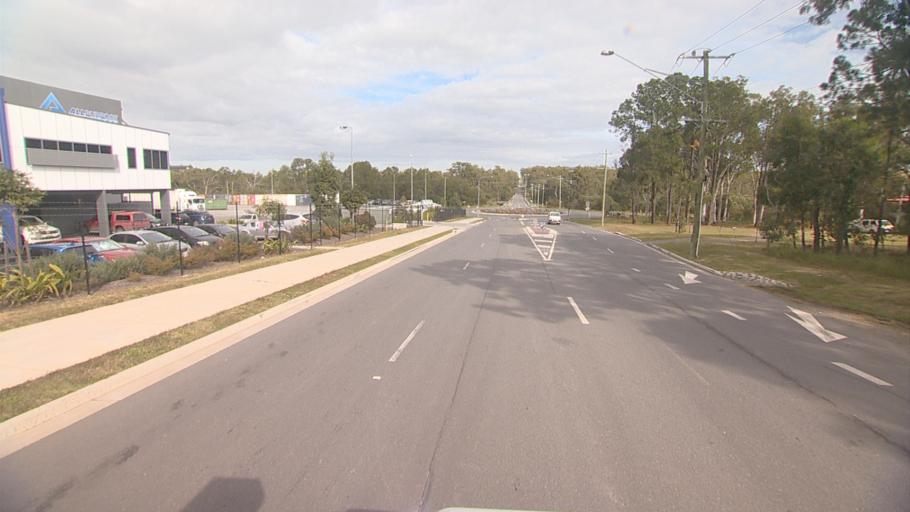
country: AU
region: Queensland
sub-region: Logan
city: Woodridge
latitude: -27.6517
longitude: 153.0895
